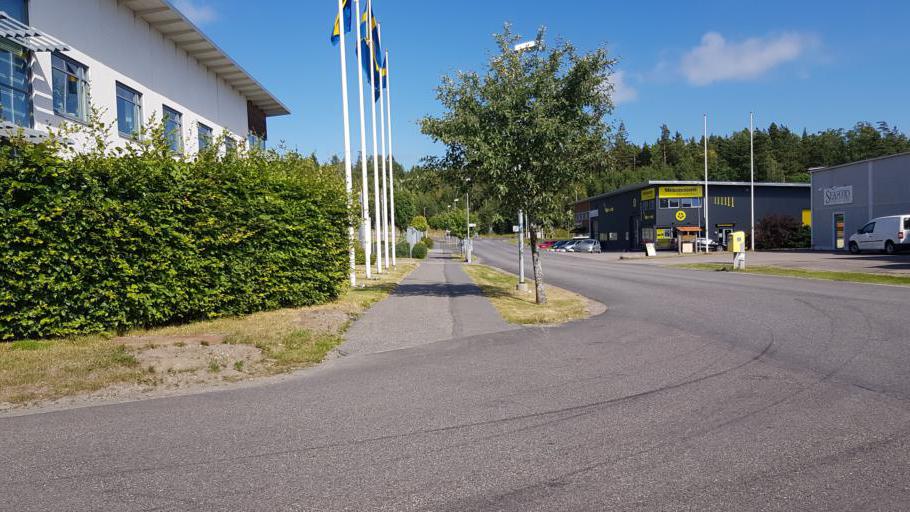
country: SE
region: Vaestra Goetaland
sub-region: Partille Kommun
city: Ojersjo
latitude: 57.6797
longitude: 12.0921
